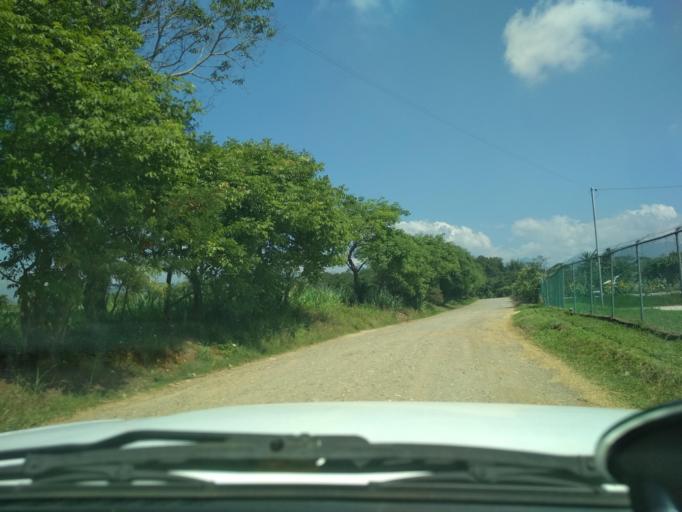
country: MX
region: Veracruz
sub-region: Fortin
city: Fraccionamiento Villas de la Llave
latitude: 18.9165
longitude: -96.9856
